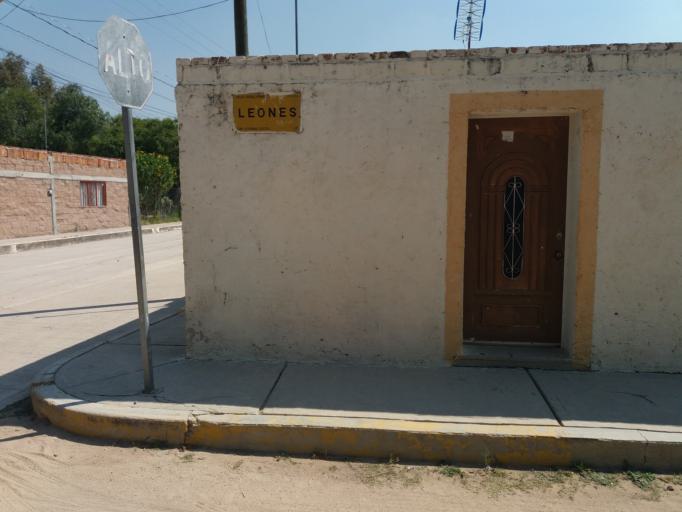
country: MX
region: Aguascalientes
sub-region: Aguascalientes
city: Penuelas (El Cienegal)
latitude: 21.7533
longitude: -102.2685
